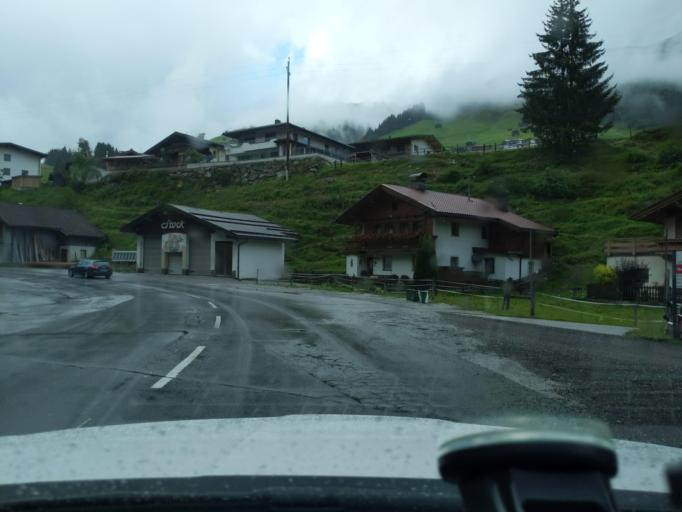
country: AT
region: Tyrol
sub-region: Politischer Bezirk Schwaz
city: Schwendau
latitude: 47.1612
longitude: 11.7473
